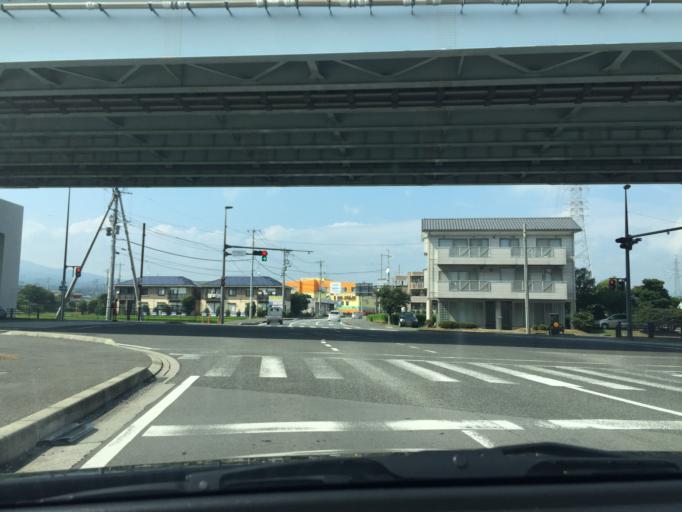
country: JP
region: Shizuoka
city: Mishima
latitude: 35.1493
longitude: 138.9044
